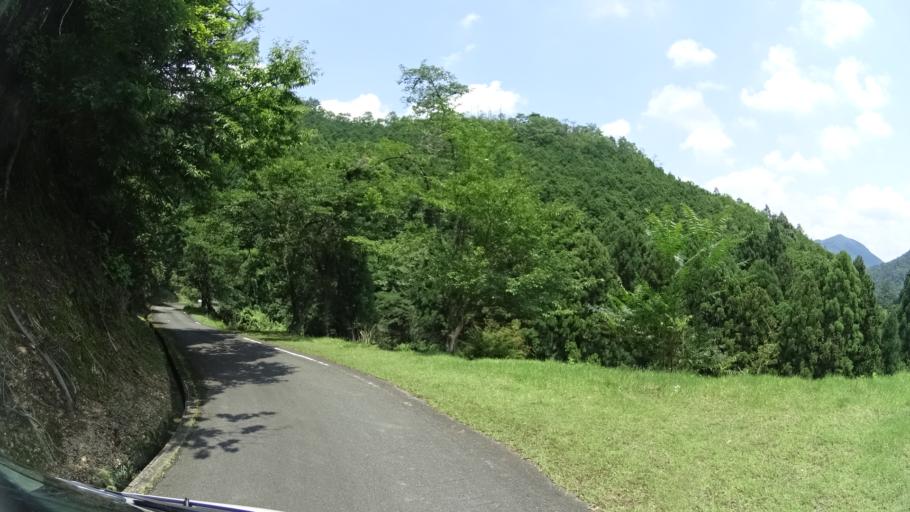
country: JP
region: Hyogo
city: Sasayama
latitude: 35.1725
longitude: 135.2020
